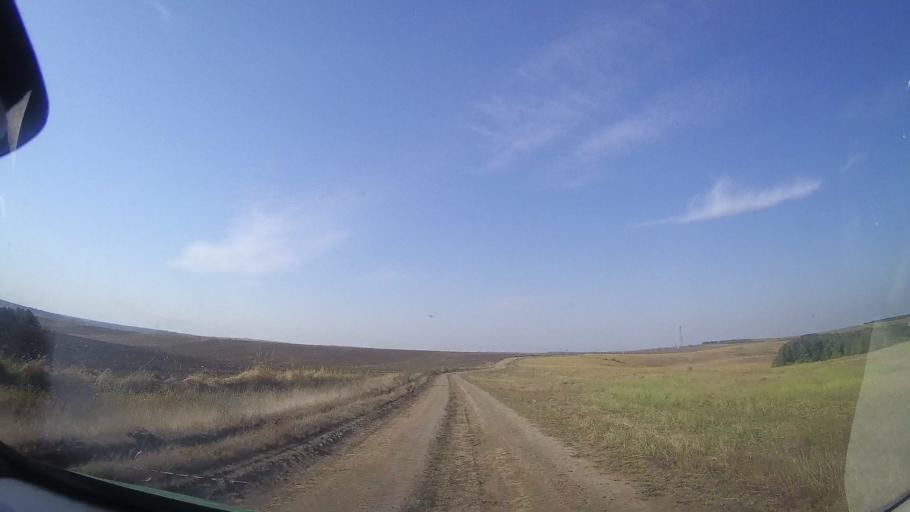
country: RO
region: Timis
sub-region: Comuna Bogda
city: Bogda
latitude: 45.8841
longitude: 21.5550
